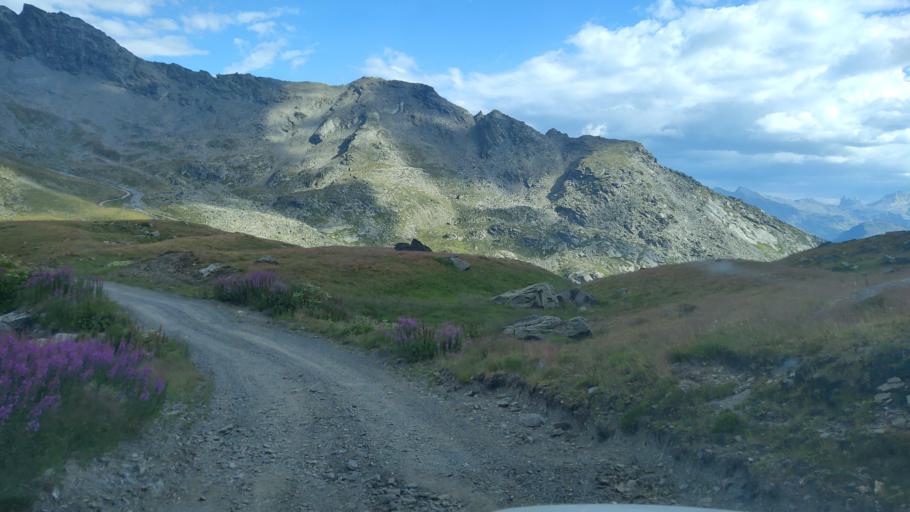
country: FR
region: Rhone-Alpes
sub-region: Departement de la Savoie
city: Val Thorens
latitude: 45.2502
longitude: 6.5646
